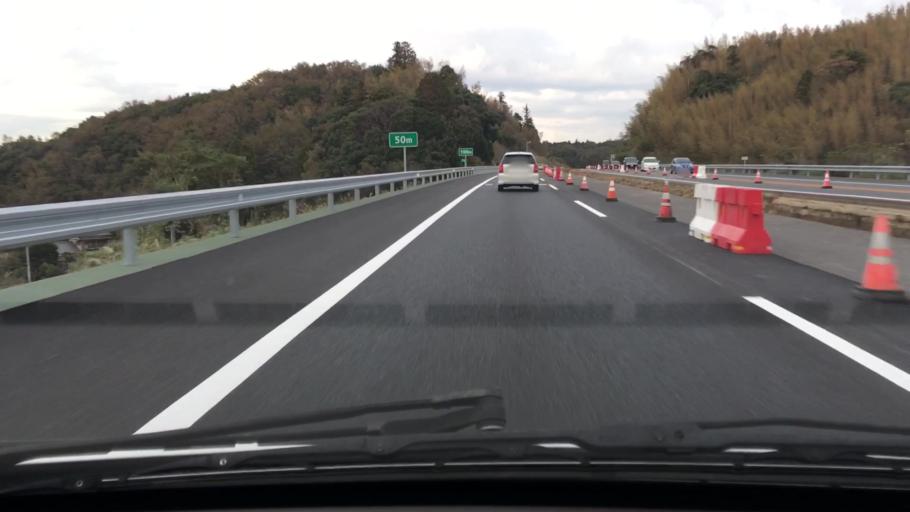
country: JP
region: Chiba
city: Kimitsu
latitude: 35.2893
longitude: 139.9292
